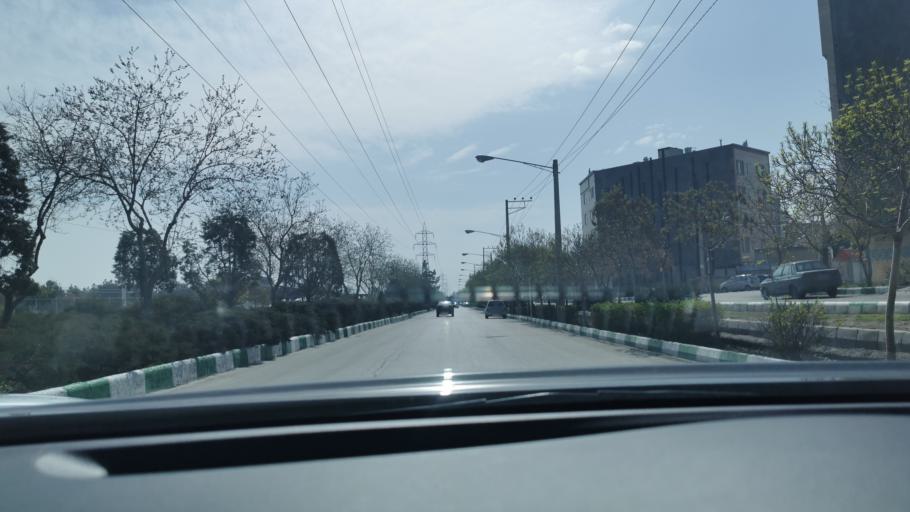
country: IR
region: Razavi Khorasan
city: Mashhad
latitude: 36.2824
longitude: 59.5451
